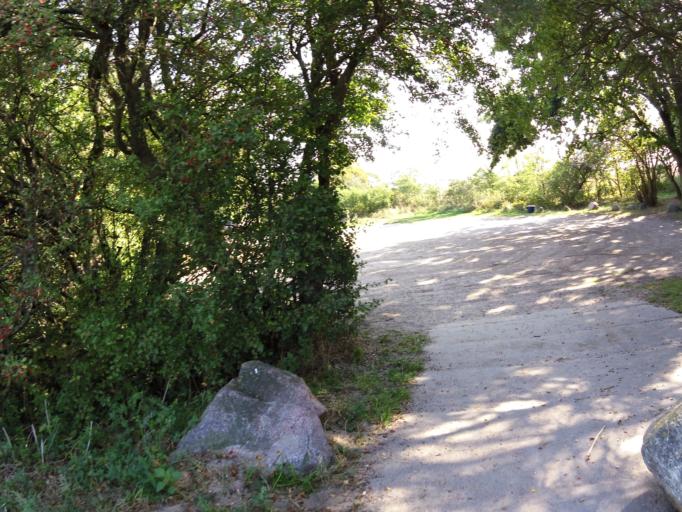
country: DE
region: Mecklenburg-Vorpommern
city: Loddin
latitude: 53.9703
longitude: 14.0454
